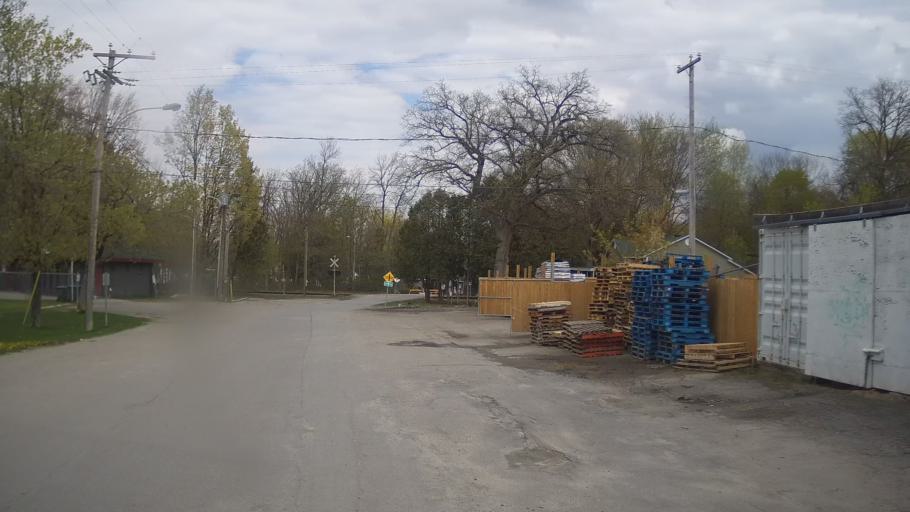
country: CA
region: Quebec
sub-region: Monteregie
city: Hudson
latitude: 45.4604
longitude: -74.1437
